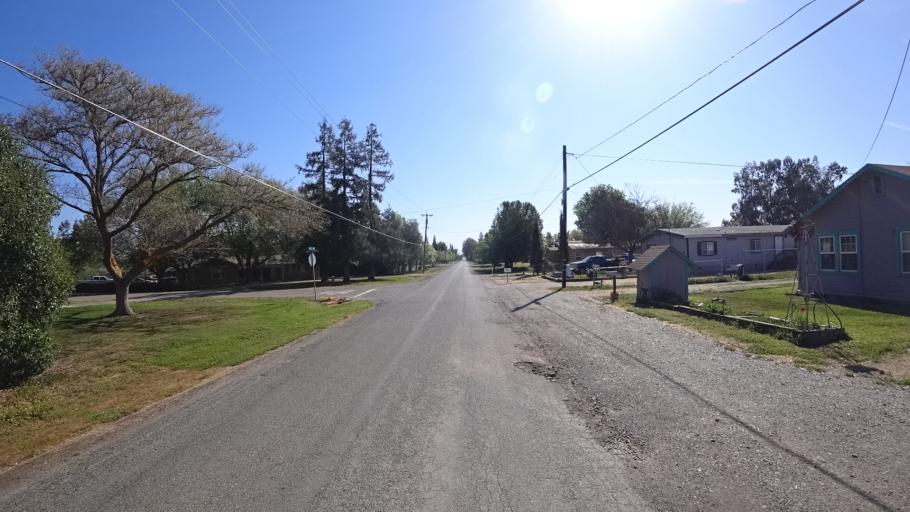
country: US
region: California
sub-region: Glenn County
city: Willows
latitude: 39.5334
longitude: -122.2046
